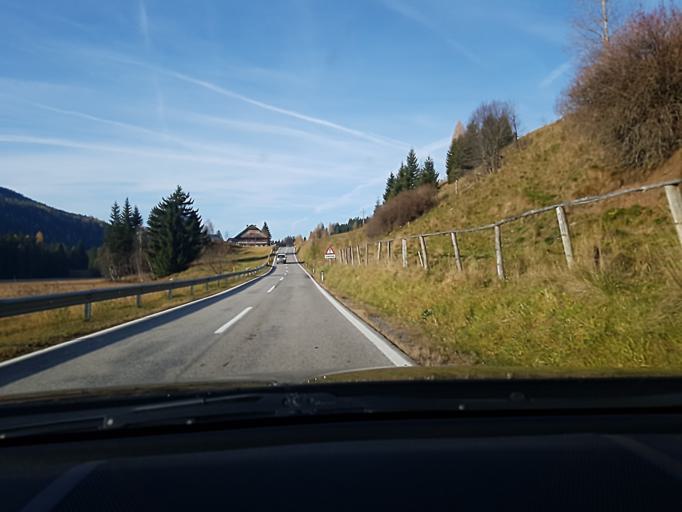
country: AT
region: Styria
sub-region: Politischer Bezirk Murau
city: Krakauschatten
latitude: 47.1513
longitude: 13.9411
